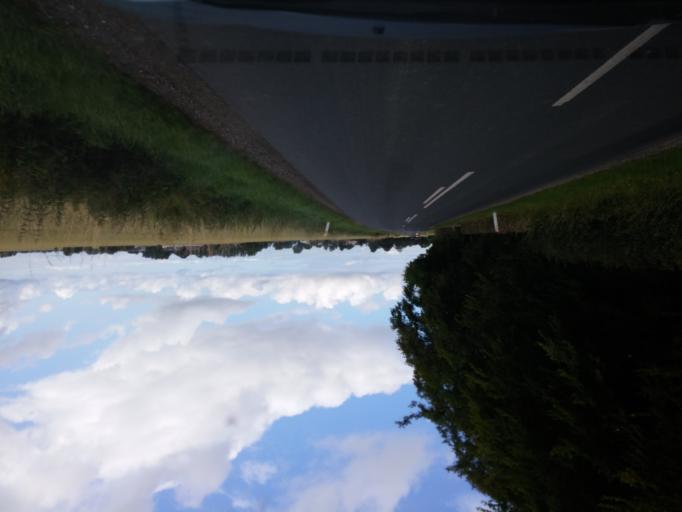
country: DK
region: South Denmark
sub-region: Kerteminde Kommune
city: Kerteminde
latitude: 55.4255
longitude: 10.6156
